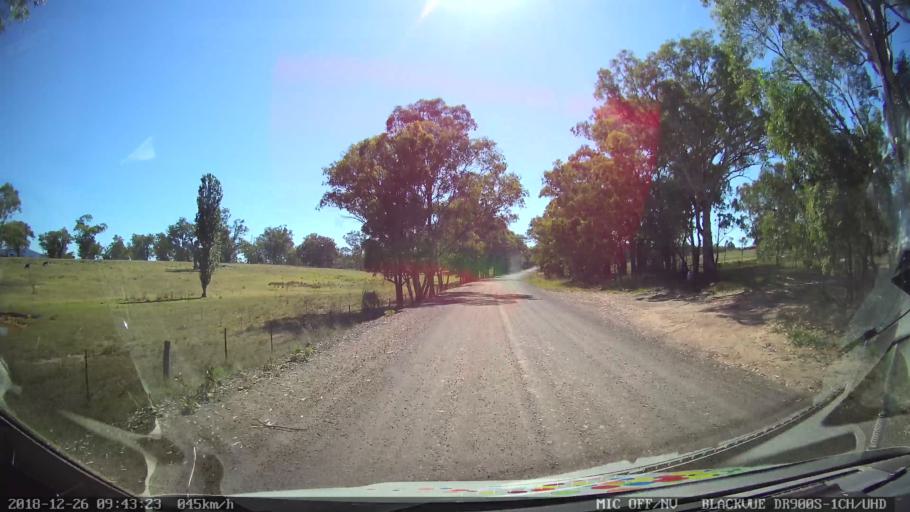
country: AU
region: New South Wales
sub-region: Mid-Western Regional
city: Kandos
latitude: -32.9544
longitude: 150.0893
